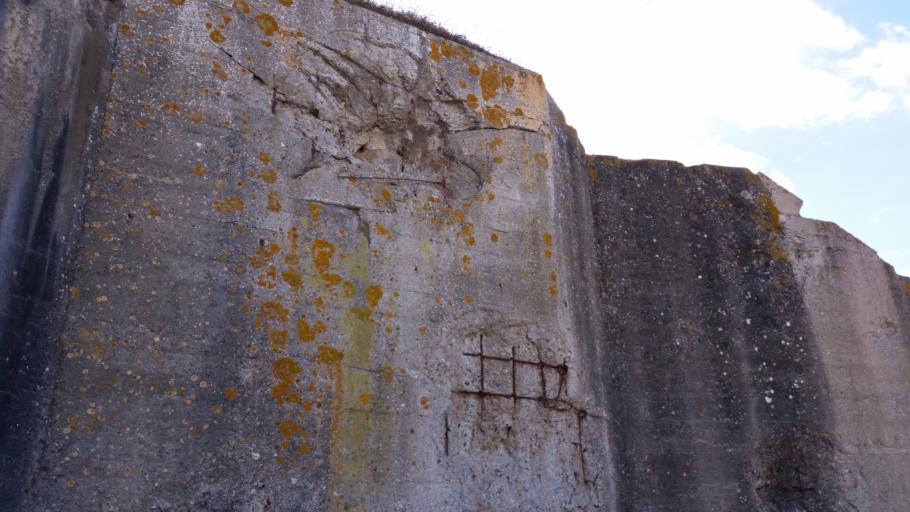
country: FR
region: Lower Normandy
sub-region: Departement de la Manche
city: Sainte-Mere-Eglise
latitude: 49.4463
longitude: -1.2110
